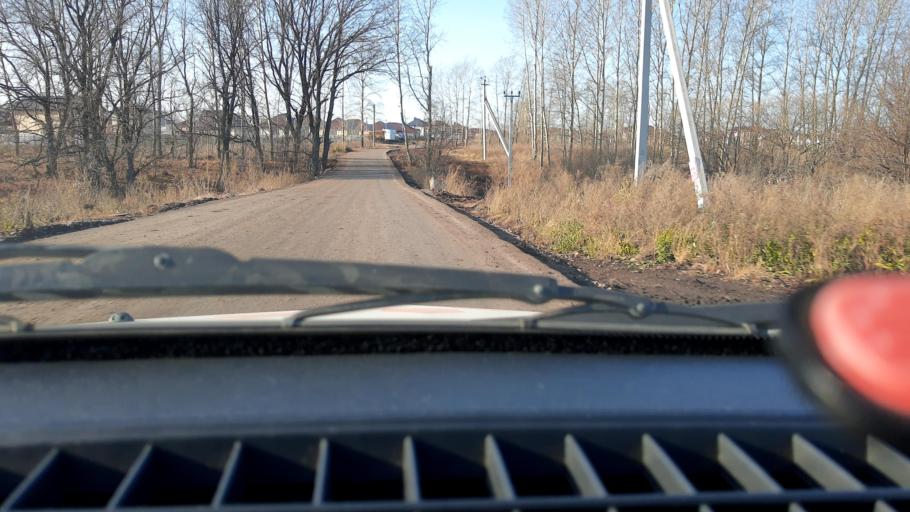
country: RU
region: Bashkortostan
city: Kabakovo
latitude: 54.6239
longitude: 56.1442
